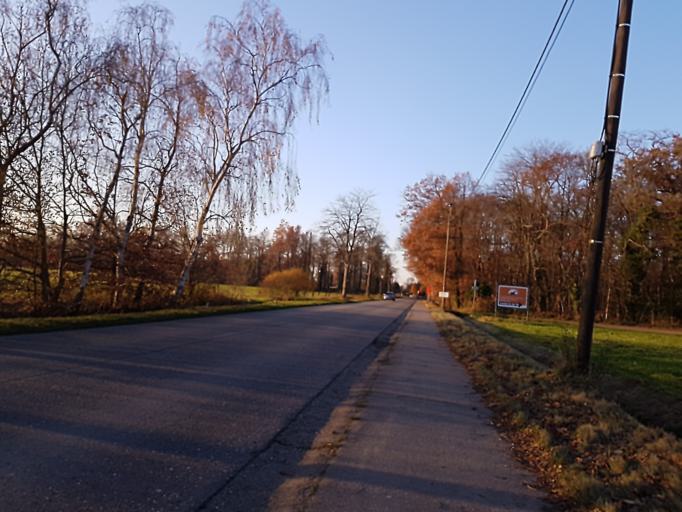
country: BE
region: Flanders
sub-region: Provincie Vlaams-Brabant
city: Boortmeerbeek
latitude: 50.9950
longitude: 4.5906
